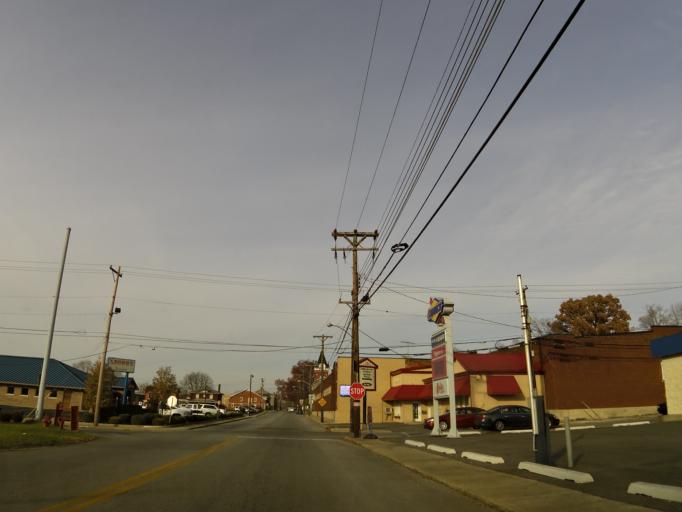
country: US
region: Kentucky
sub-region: Harrison County
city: Cynthiana
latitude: 38.3873
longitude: -84.2944
